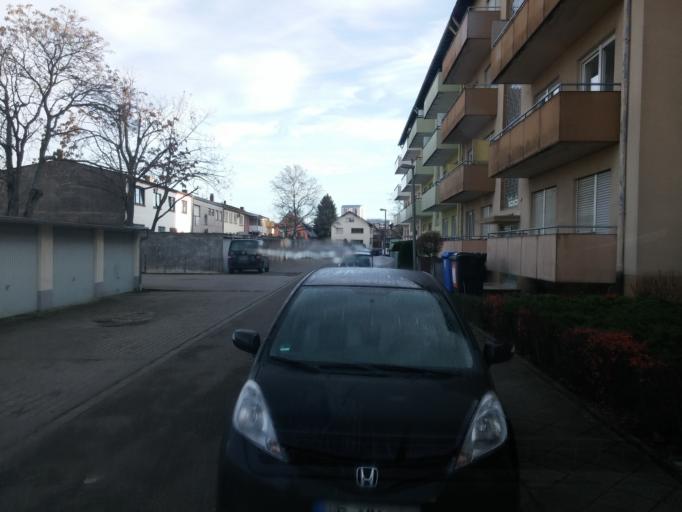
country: DE
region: Baden-Wuerttemberg
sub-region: Karlsruhe Region
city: Karlsruhe
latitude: 49.0134
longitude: 8.4316
